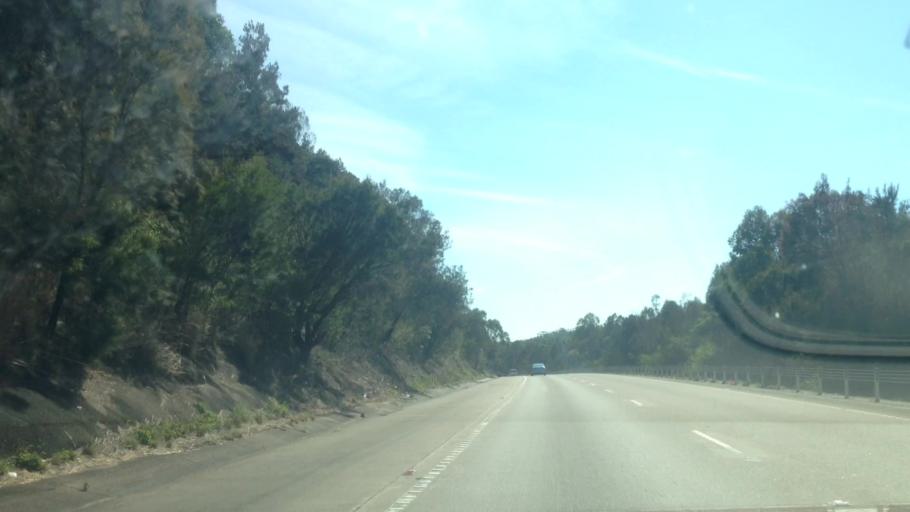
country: AU
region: New South Wales
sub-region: Lake Macquarie Shire
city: Fennell Bay
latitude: -32.9759
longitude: 151.5303
